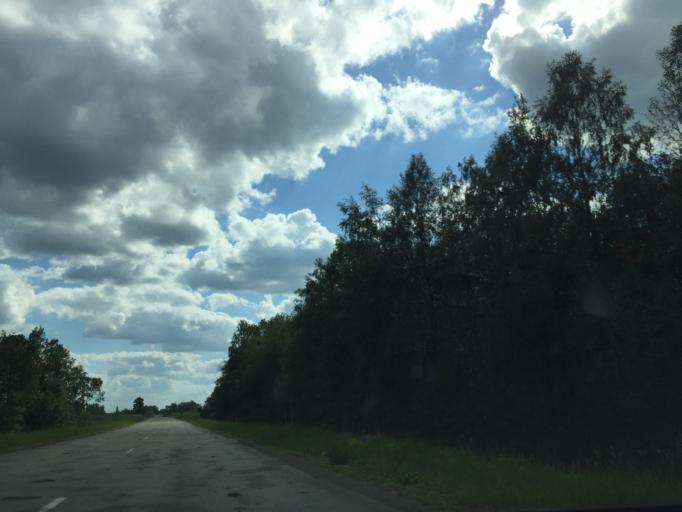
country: LV
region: Jaunpils
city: Jaunpils
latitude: 56.8632
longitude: 23.0572
